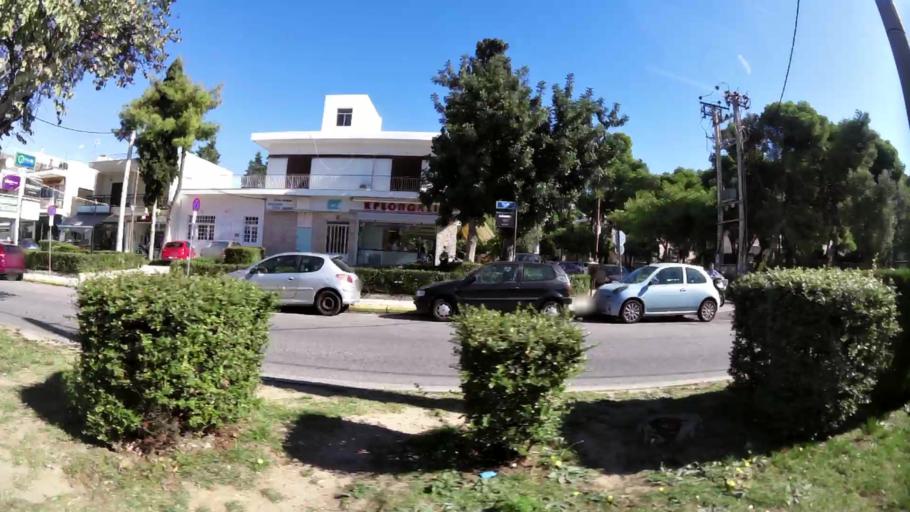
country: GR
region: Attica
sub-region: Nomarchia Athinas
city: Kifisia
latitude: 38.0908
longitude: 23.7972
